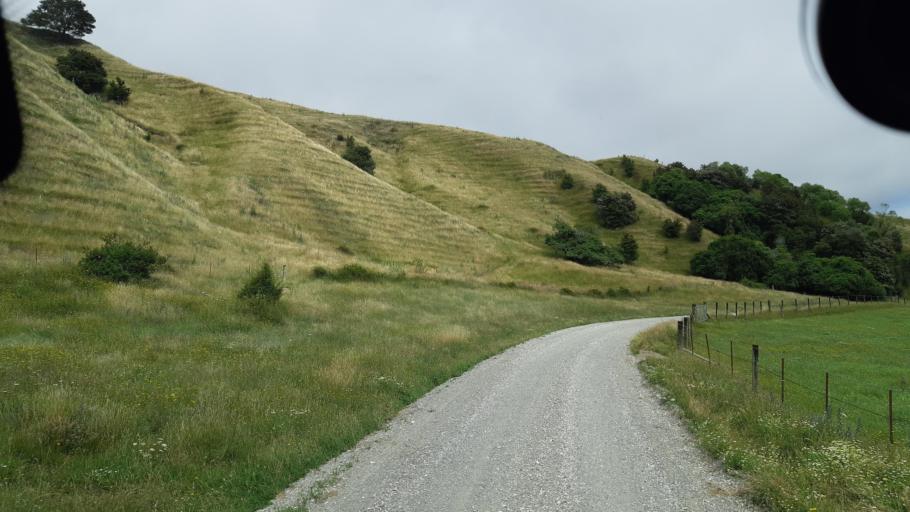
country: NZ
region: Marlborough
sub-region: Marlborough District
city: Blenheim
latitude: -41.9744
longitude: 173.9956
